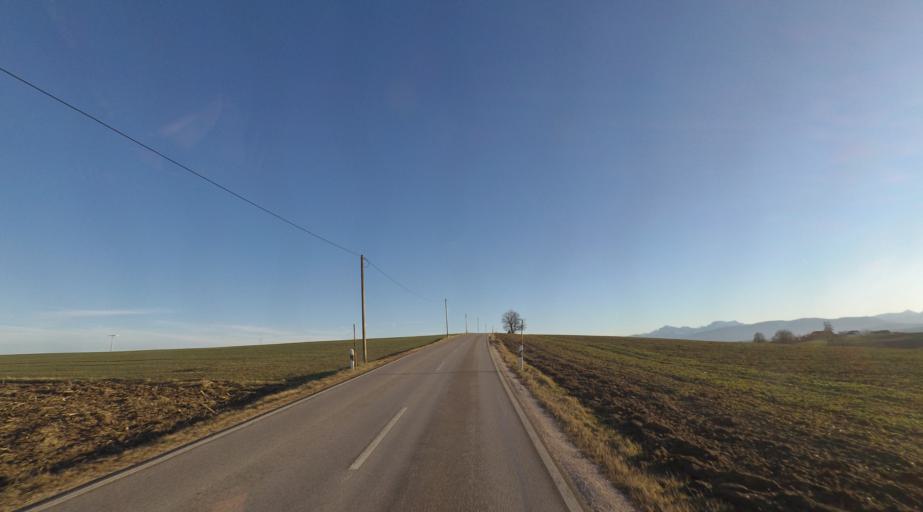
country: DE
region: Bavaria
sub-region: Upper Bavaria
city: Taching am See
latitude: 47.9810
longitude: 12.7763
